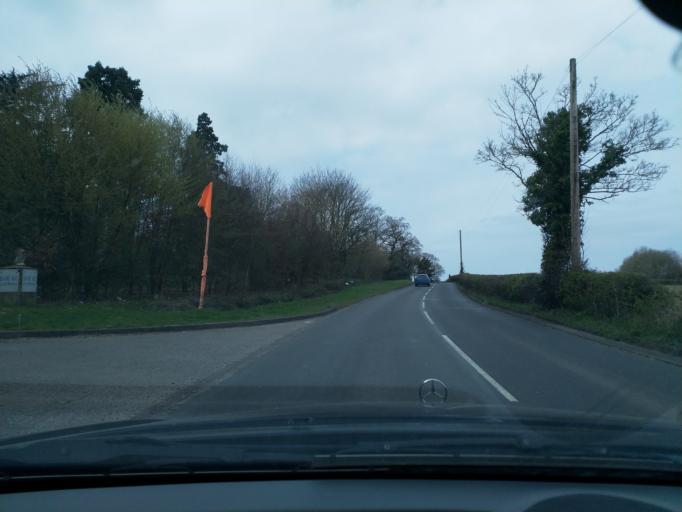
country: GB
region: England
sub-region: Warwickshire
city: Royal Leamington Spa
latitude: 52.3233
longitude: -1.5450
